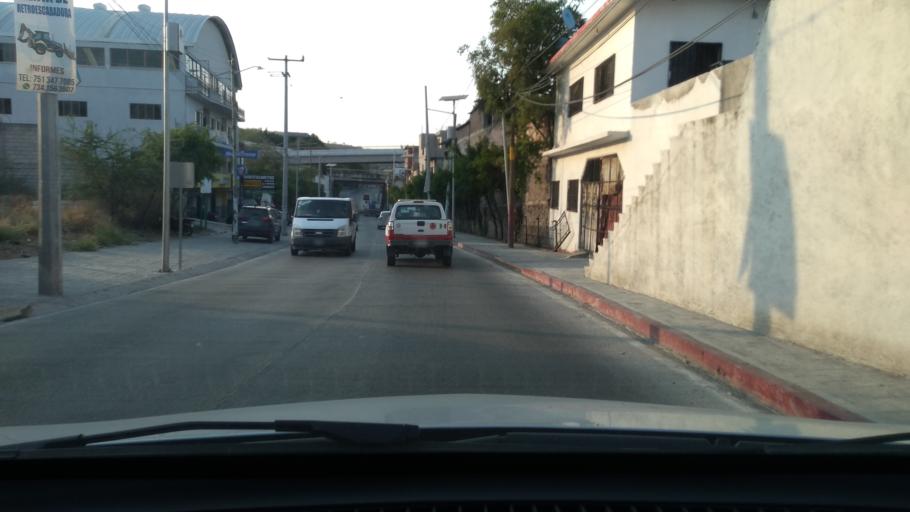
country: MX
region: Morelos
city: Puente de Ixtla
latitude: 18.6303
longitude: -99.3229
